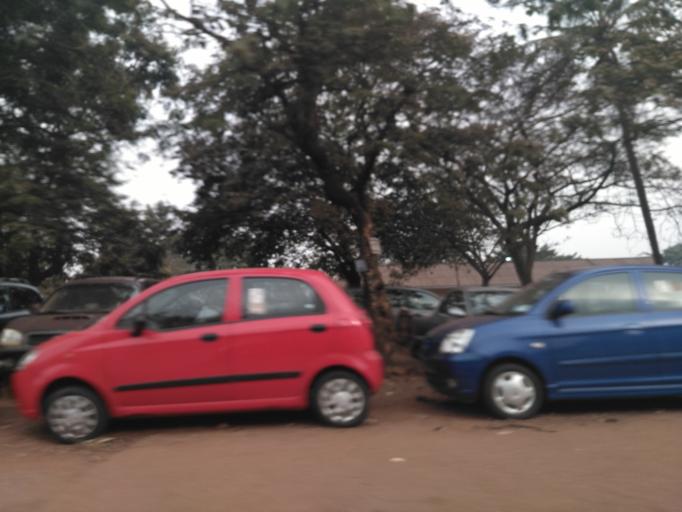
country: GH
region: Ashanti
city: Kumasi
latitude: 6.7095
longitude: -1.6336
